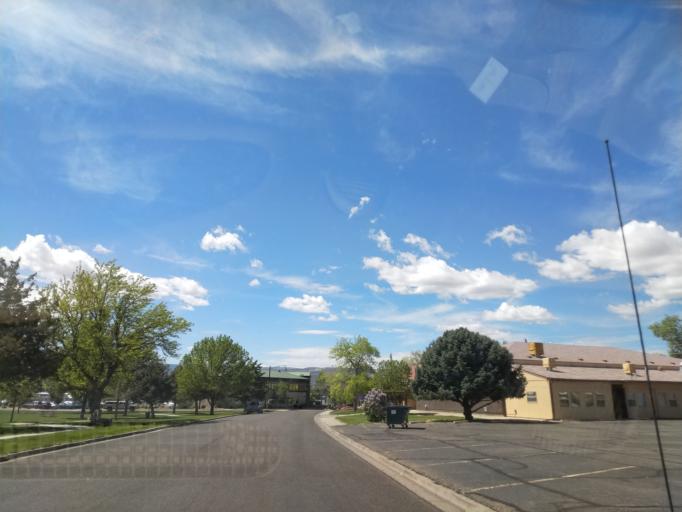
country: US
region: Colorado
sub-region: Mesa County
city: Grand Junction
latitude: 39.0798
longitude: -108.5697
